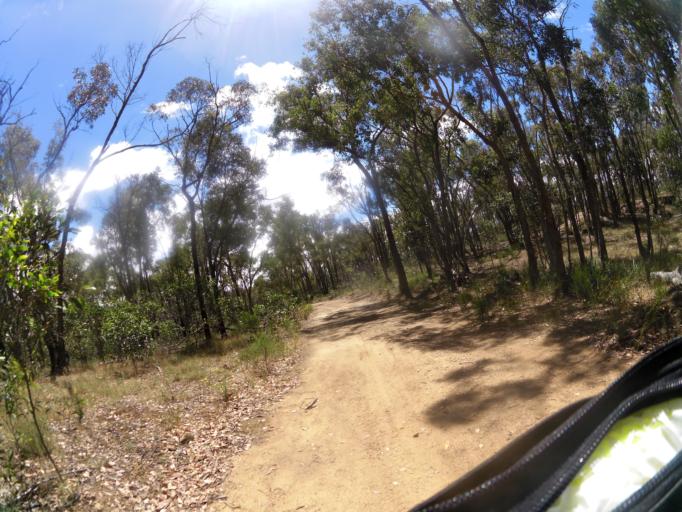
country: AU
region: Victoria
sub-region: Mount Alexander
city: Castlemaine
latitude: -37.0658
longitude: 144.2656
